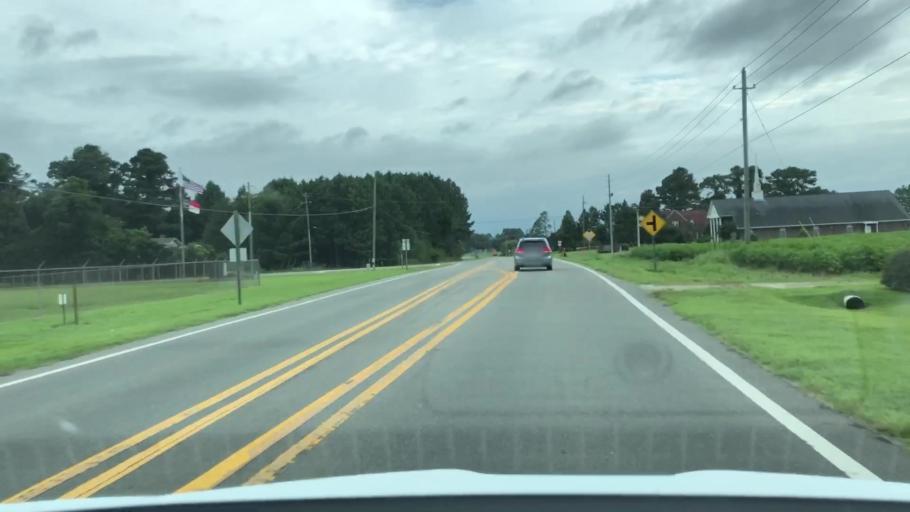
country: US
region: North Carolina
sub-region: Lenoir County
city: Kinston
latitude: 35.2295
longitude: -77.5750
